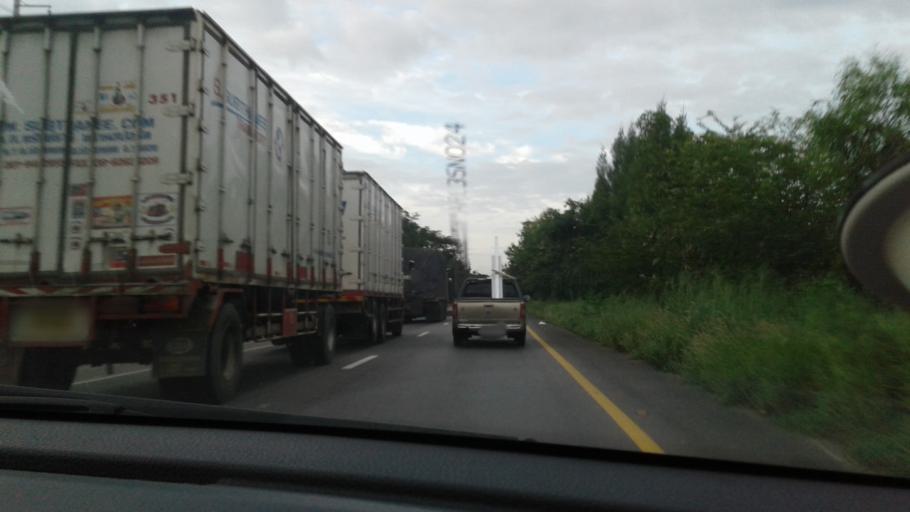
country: TH
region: Prachuap Khiri Khan
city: Hua Hin
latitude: 12.5609
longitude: 99.8701
